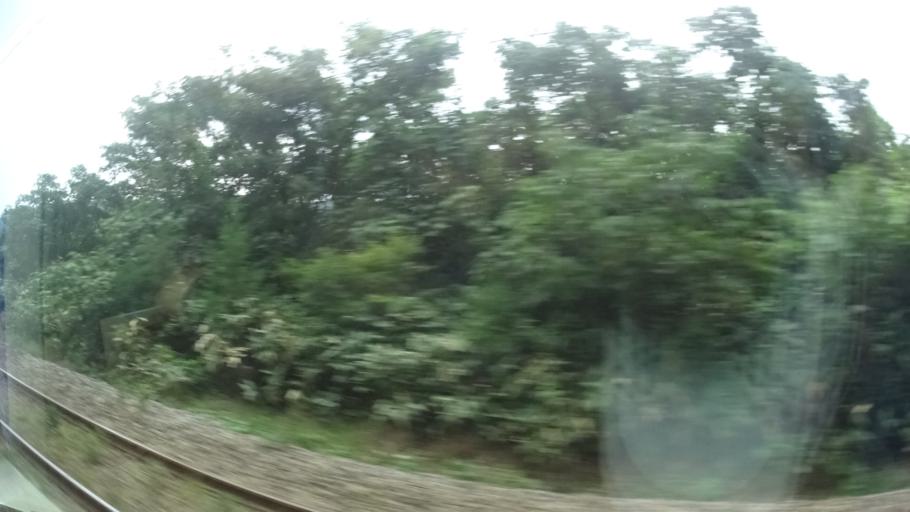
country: JP
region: Yamagata
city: Tsuruoka
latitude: 38.7032
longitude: 139.7158
